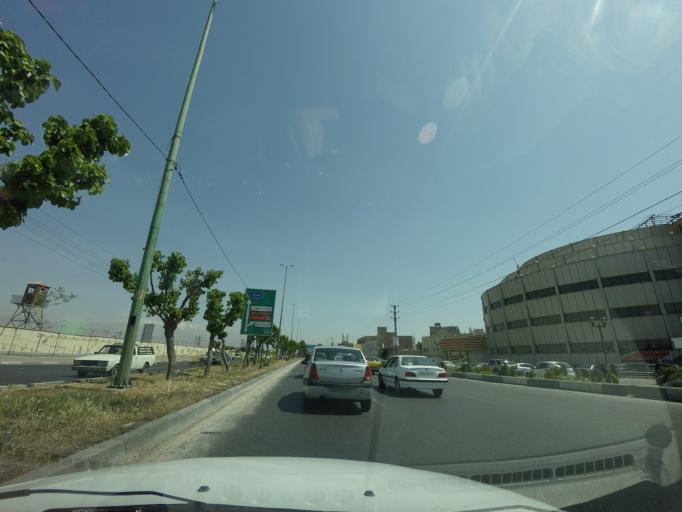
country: IR
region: Tehran
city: Eslamshahr
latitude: 35.6094
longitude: 51.3089
